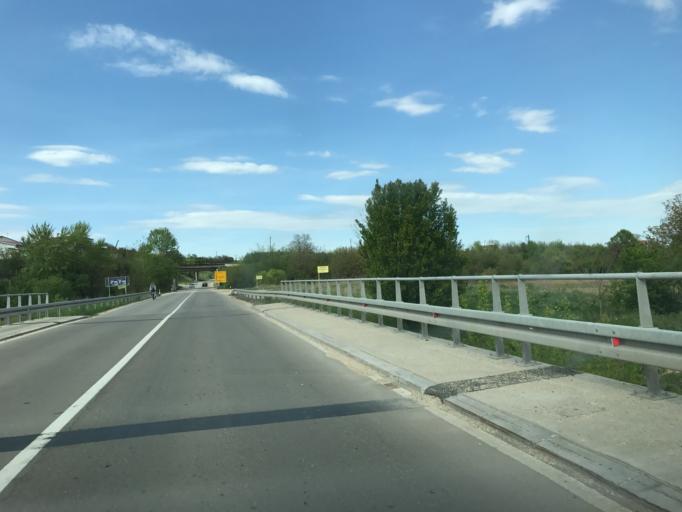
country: RS
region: Central Serbia
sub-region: Zajecarski Okrug
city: Zajecar
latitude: 43.9199
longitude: 22.2948
